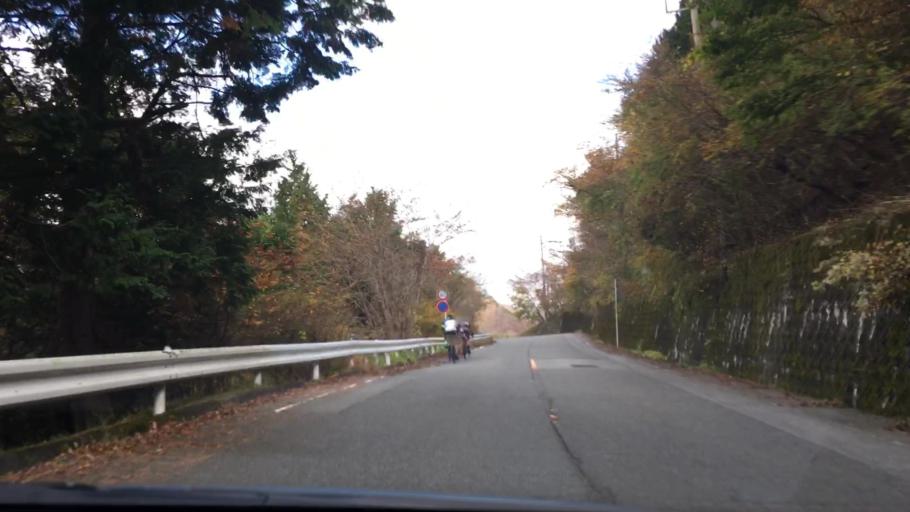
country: JP
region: Shizuoka
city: Gotemba
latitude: 35.3916
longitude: 138.9426
